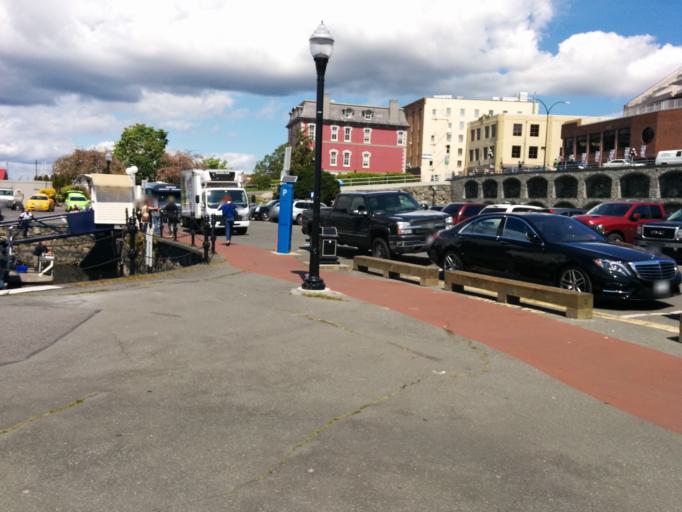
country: CA
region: British Columbia
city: Victoria
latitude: 48.4234
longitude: -123.3703
